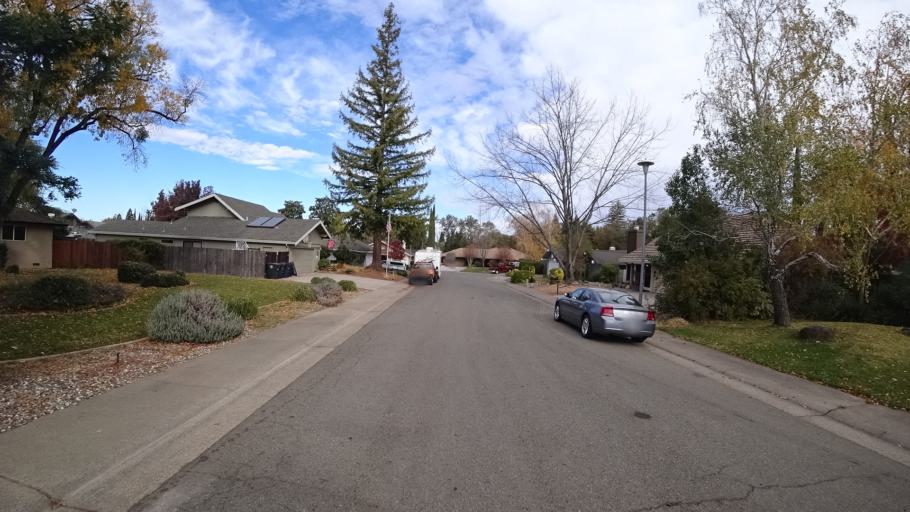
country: US
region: California
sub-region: Sacramento County
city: Citrus Heights
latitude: 38.7143
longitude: -121.2458
